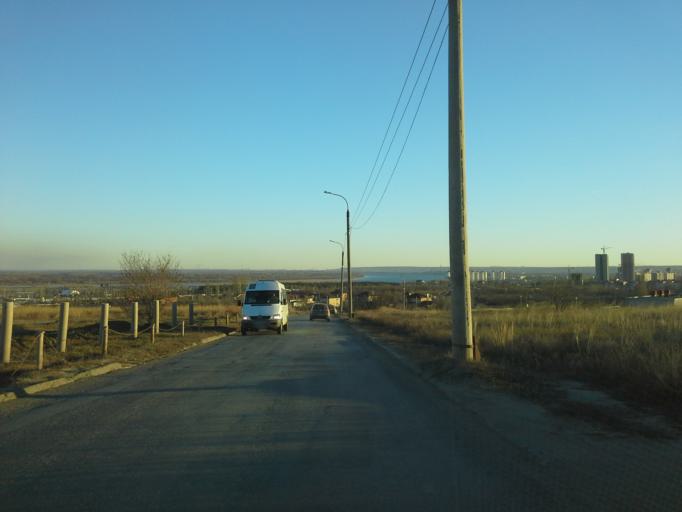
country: RU
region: Volgograd
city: Volgograd
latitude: 48.6402
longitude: 44.4215
